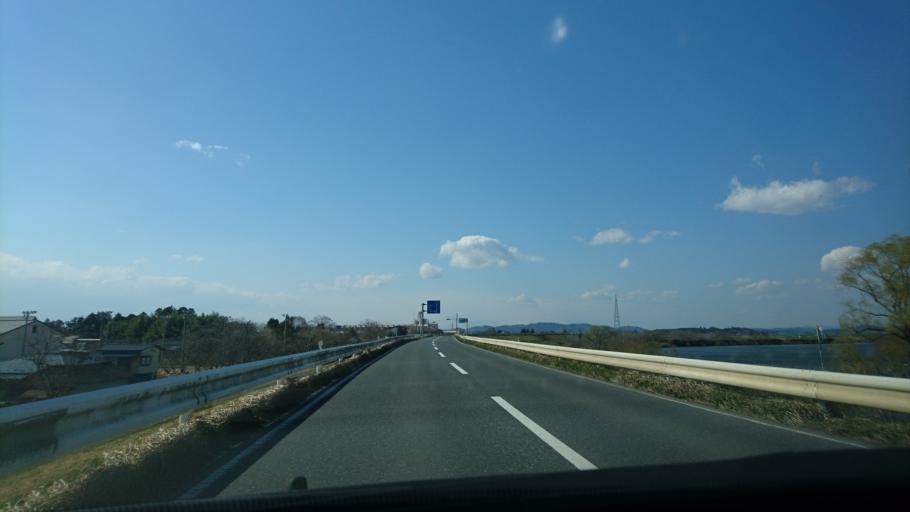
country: JP
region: Miyagi
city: Wakuya
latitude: 38.7064
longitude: 141.2693
